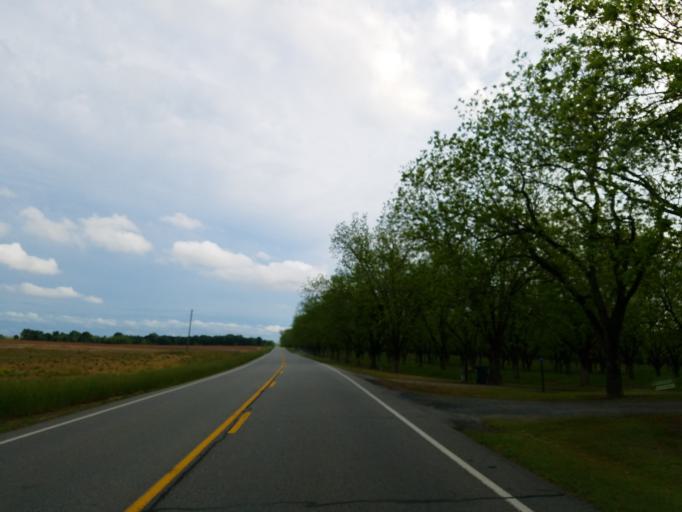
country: US
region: Georgia
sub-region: Dooly County
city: Unadilla
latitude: 32.2182
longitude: -83.7592
